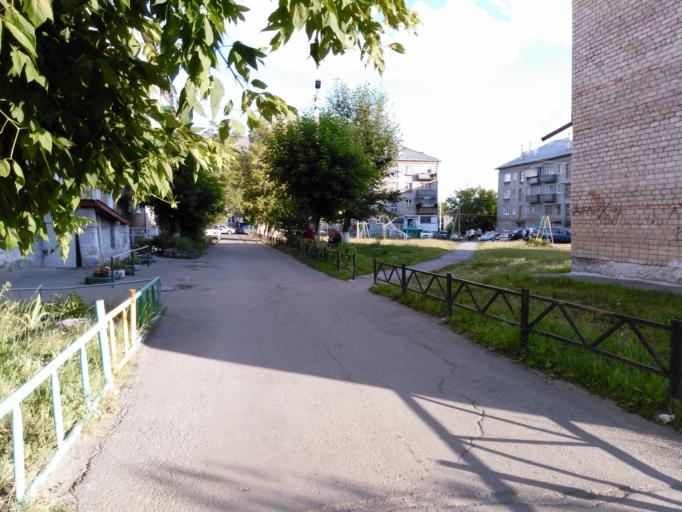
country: RU
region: Bashkortostan
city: Uchaly
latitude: 54.3163
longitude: 59.3842
